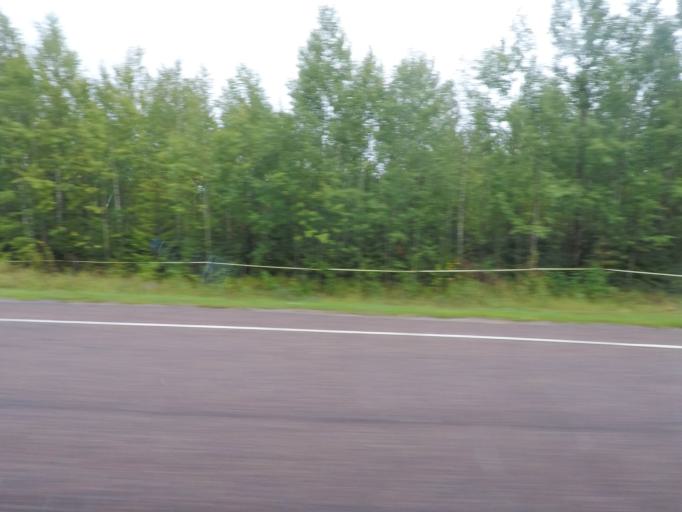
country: FI
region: Northern Savo
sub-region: Varkaus
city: Varkaus
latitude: 62.3835
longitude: 27.8093
